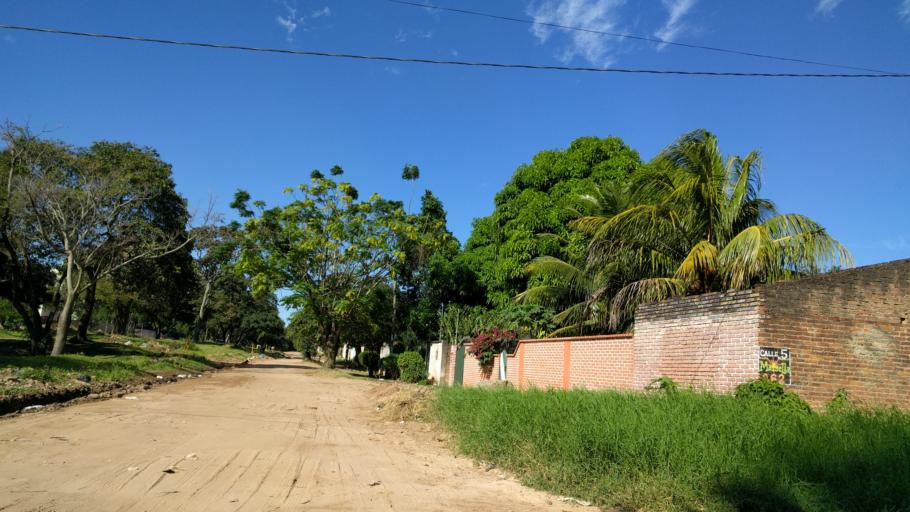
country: BO
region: Santa Cruz
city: Santa Cruz de la Sierra
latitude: -17.7899
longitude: -63.2248
